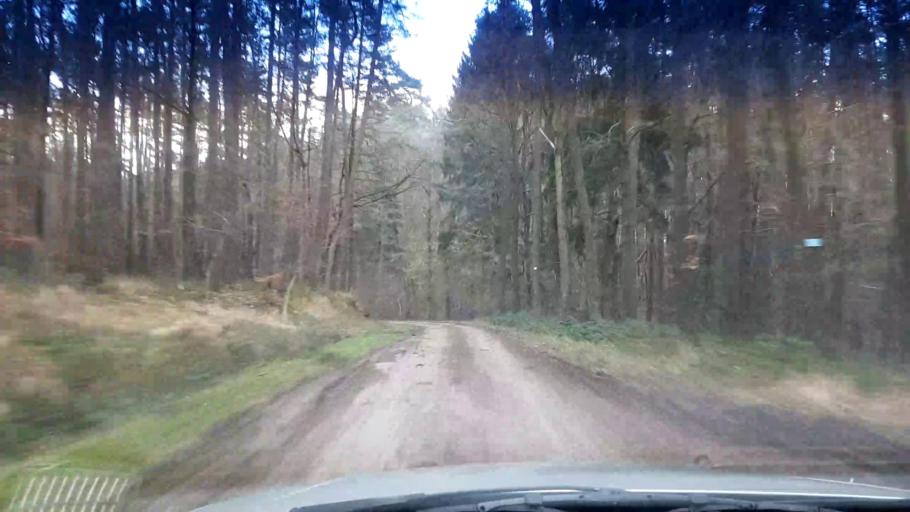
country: DE
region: Bavaria
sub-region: Upper Franconia
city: Lauter
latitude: 49.9451
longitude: 10.7832
